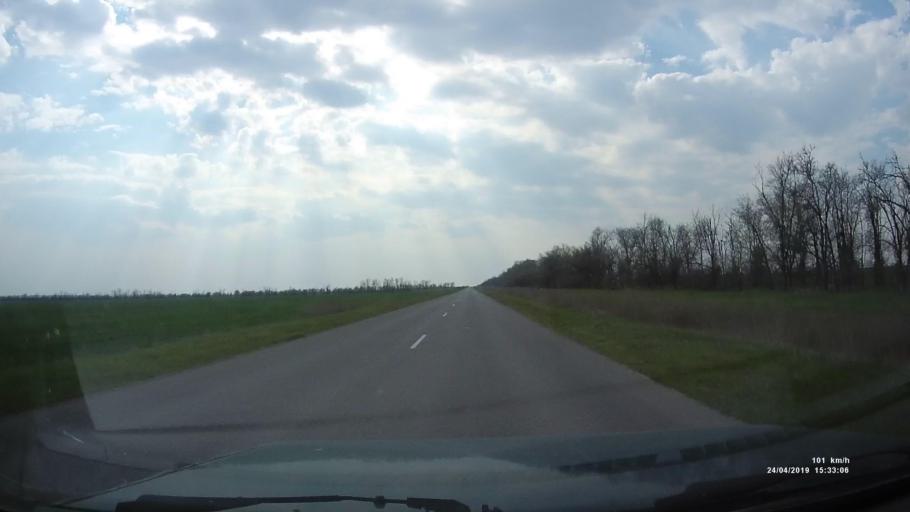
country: RU
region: Rostov
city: Remontnoye
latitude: 46.5992
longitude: 42.9458
